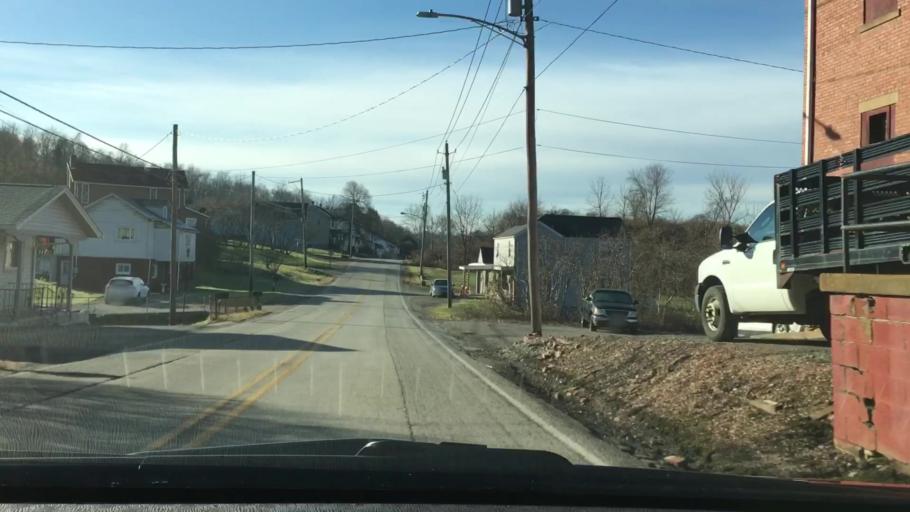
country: US
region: Pennsylvania
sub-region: Westmoreland County
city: Irwin
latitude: 40.2832
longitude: -79.6927
